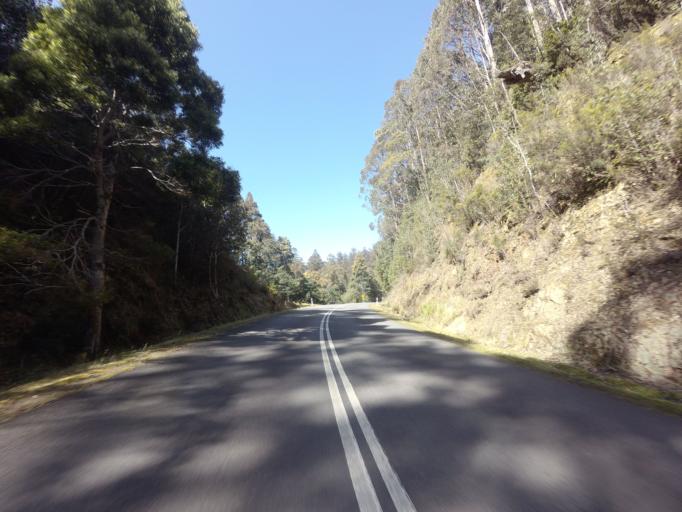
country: AU
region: Tasmania
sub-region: Derwent Valley
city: New Norfolk
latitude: -42.7441
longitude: 146.5008
